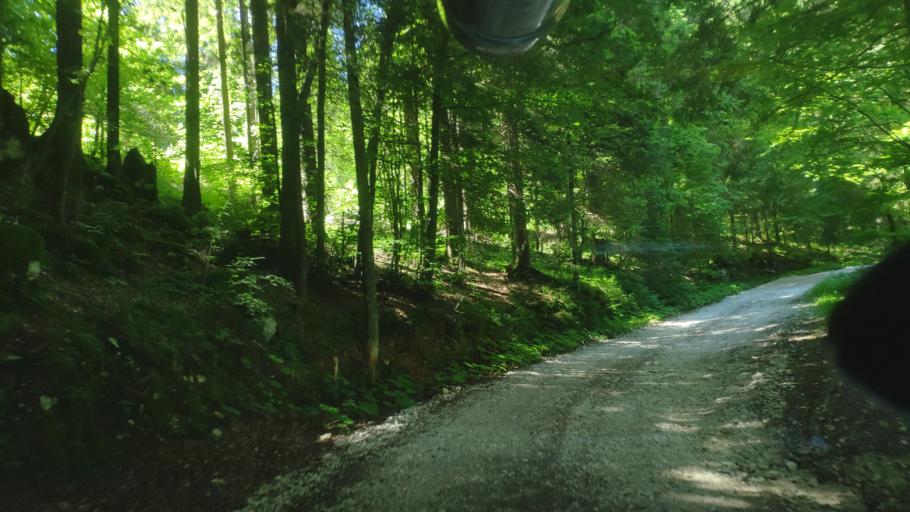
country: IT
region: Veneto
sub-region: Provincia di Vicenza
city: Cogollo del Cengio
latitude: 45.8139
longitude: 11.4520
